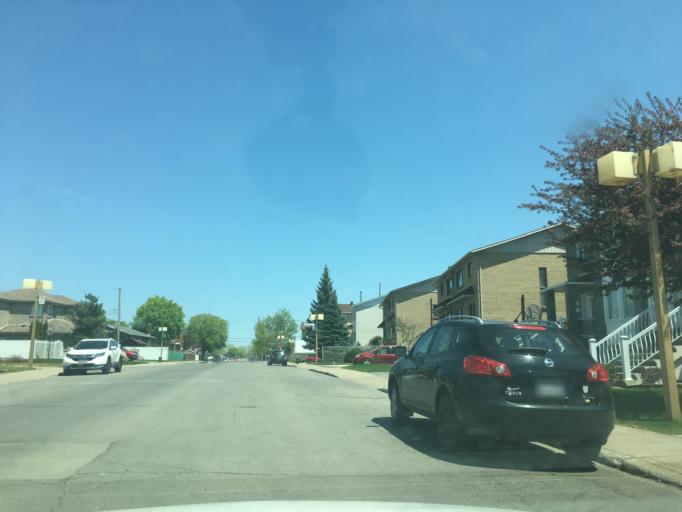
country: CA
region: Quebec
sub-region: Montreal
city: Saint-Leonard
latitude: 45.6268
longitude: -73.5901
